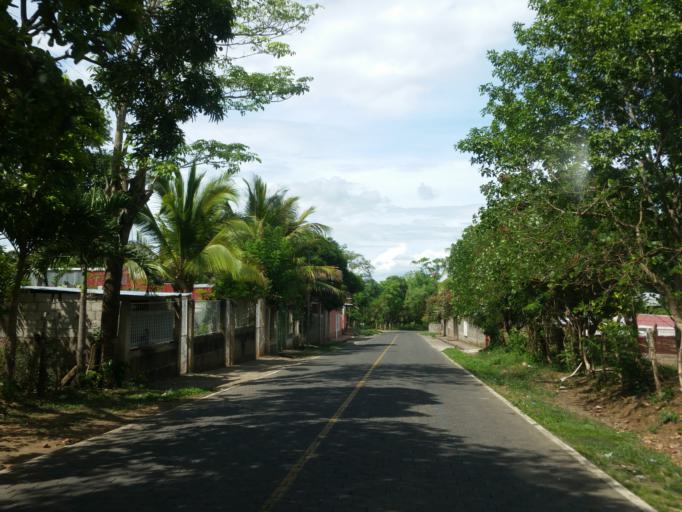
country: NI
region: Masaya
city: Masaya
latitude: 11.9618
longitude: -86.0419
